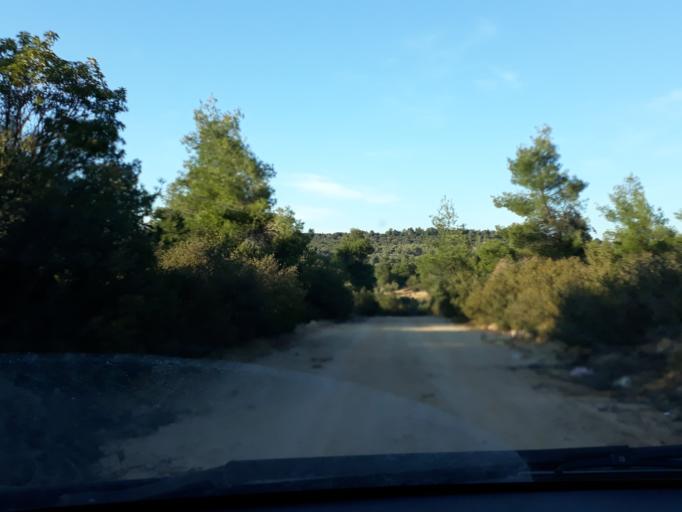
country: GR
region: Central Greece
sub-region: Nomos Voiotias
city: Asopia
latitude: 38.2624
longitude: 23.5352
